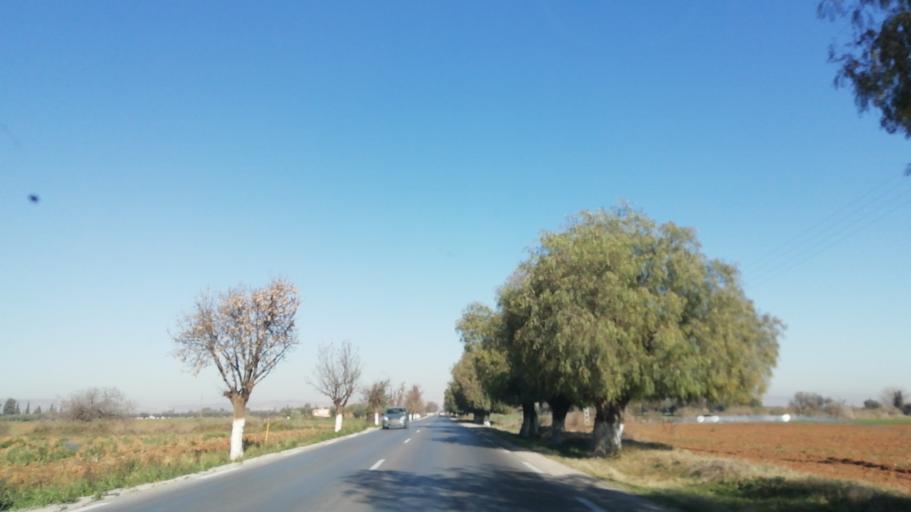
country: DZ
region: Mascara
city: Mascara
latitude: 35.2885
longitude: 0.1278
